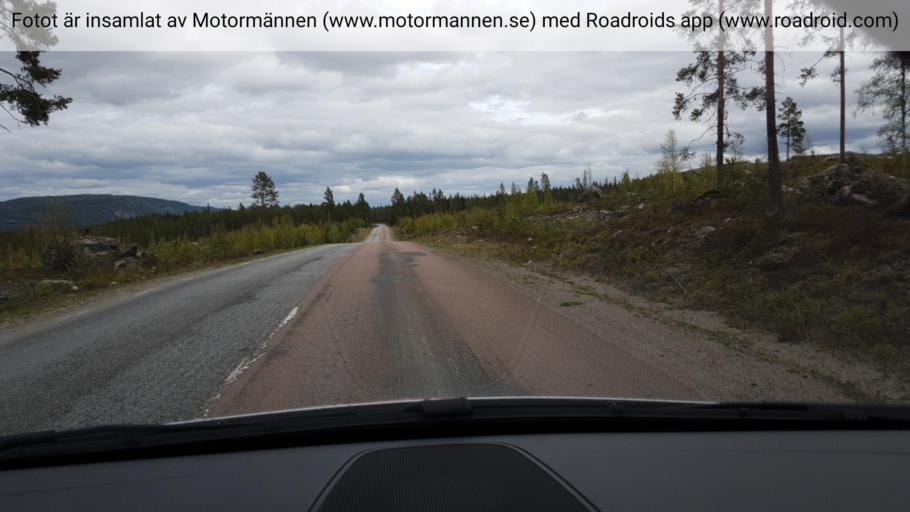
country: SE
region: Jaemtland
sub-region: Braecke Kommun
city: Braecke
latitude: 62.8556
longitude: 15.5391
